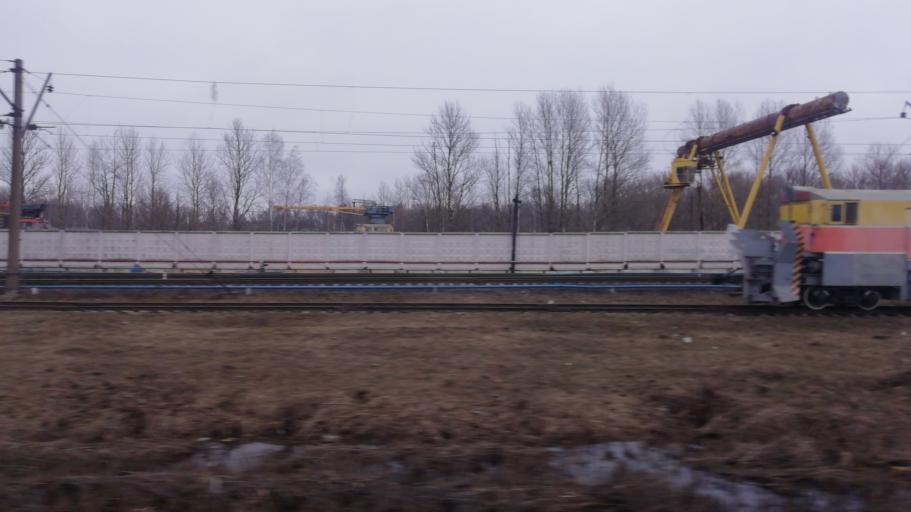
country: RU
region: St.-Petersburg
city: Kupchino
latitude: 59.8808
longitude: 30.3485
